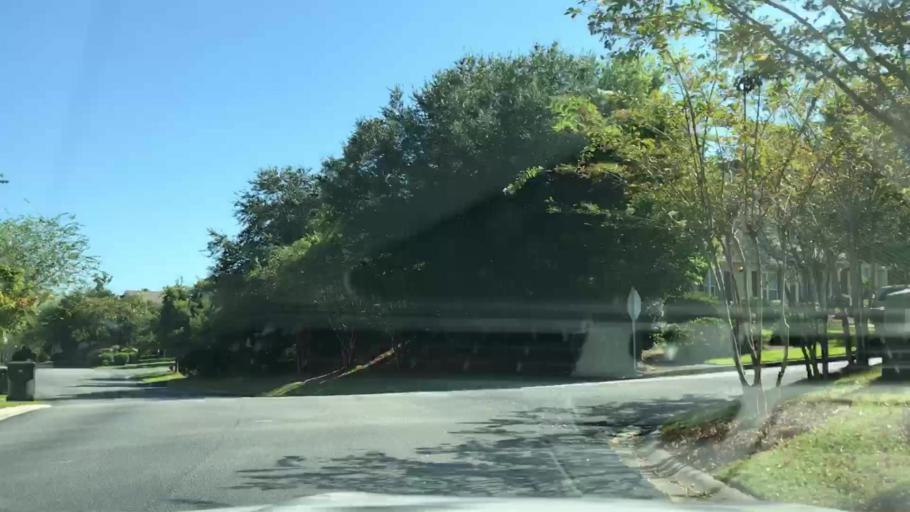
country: US
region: South Carolina
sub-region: Berkeley County
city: Sangaree
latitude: 33.0329
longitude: -80.0693
